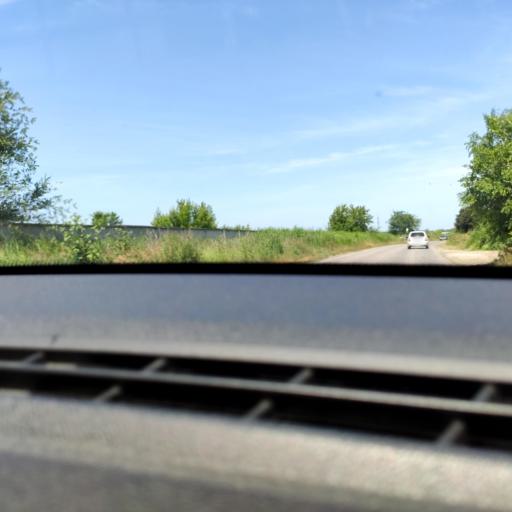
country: RU
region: Samara
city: Podstepki
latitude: 53.5932
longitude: 49.2160
